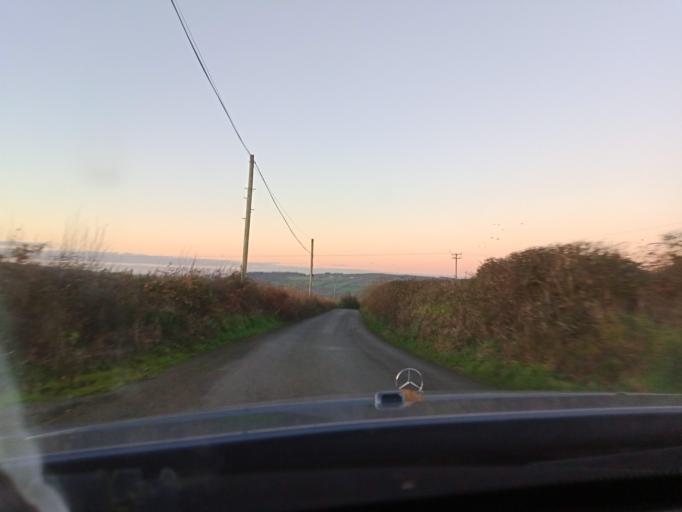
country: IE
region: Leinster
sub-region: Kilkenny
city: Thomastown
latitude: 52.4784
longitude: -7.1012
